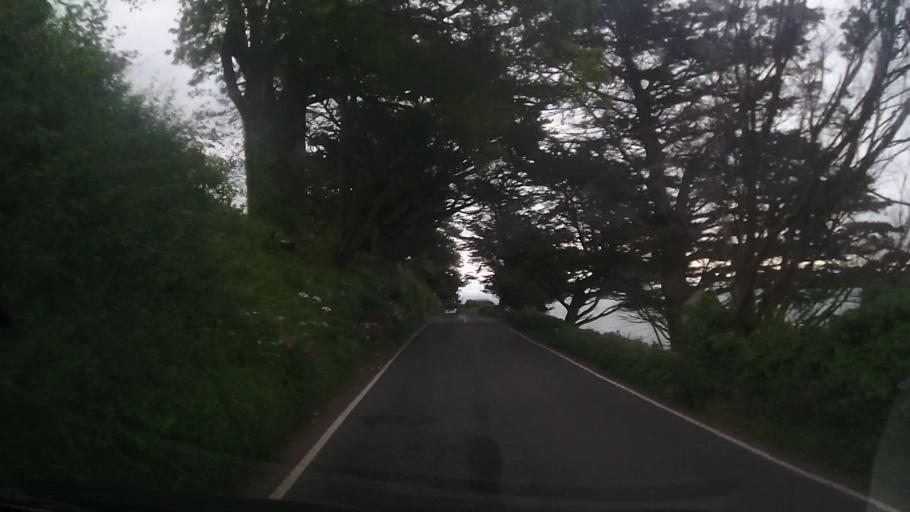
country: GB
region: England
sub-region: Devon
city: Dartmouth
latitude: 50.3154
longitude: -3.6184
